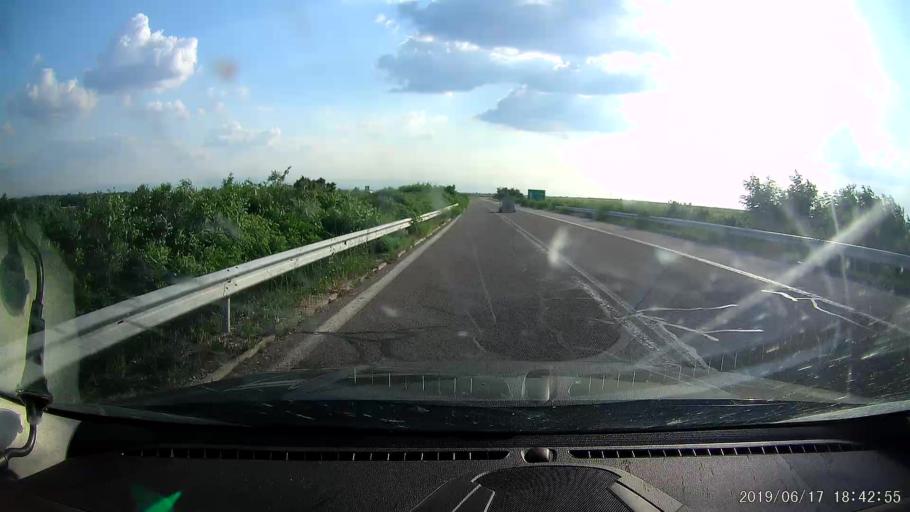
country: BG
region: Stara Zagora
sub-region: Obshtina Chirpan
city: Chirpan
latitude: 42.1946
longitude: 25.2270
